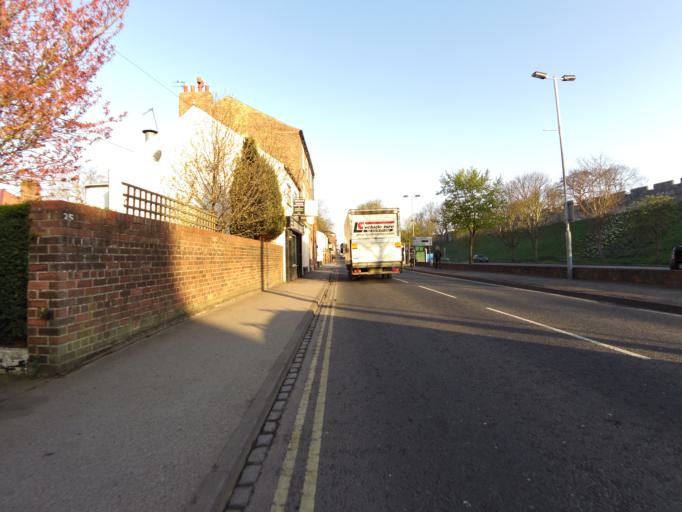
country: GB
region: England
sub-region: City of York
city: York
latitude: 53.9541
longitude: -1.0879
